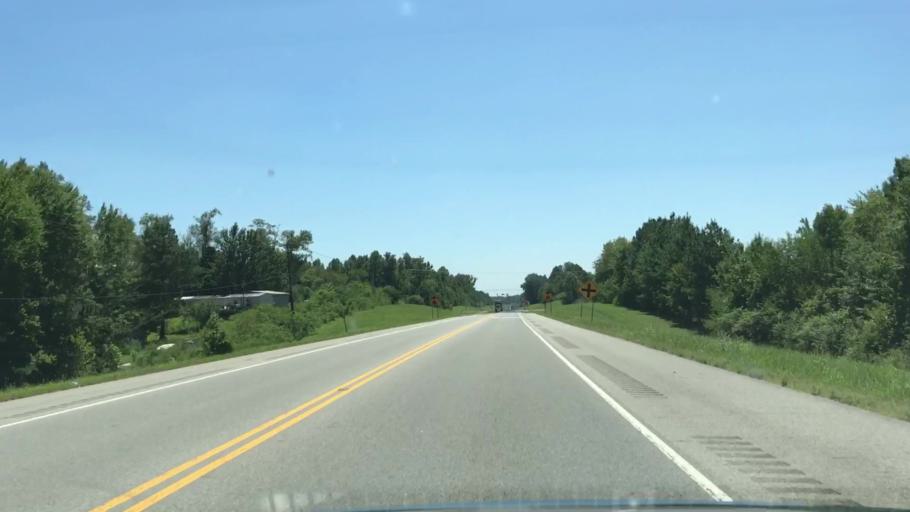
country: US
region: Tennessee
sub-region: Putnam County
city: Baxter
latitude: 36.1563
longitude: -85.6282
